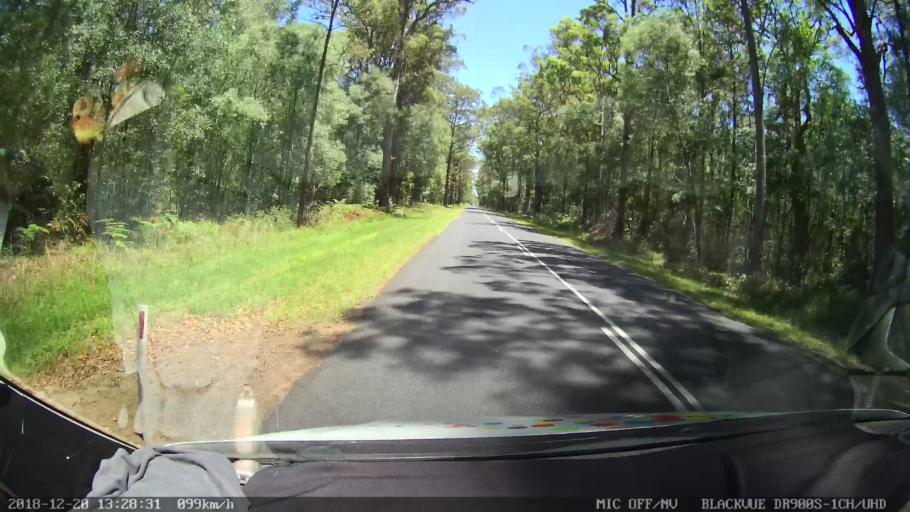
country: AU
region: New South Wales
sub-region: Clarence Valley
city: Gordon
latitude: -29.1756
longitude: 152.9898
